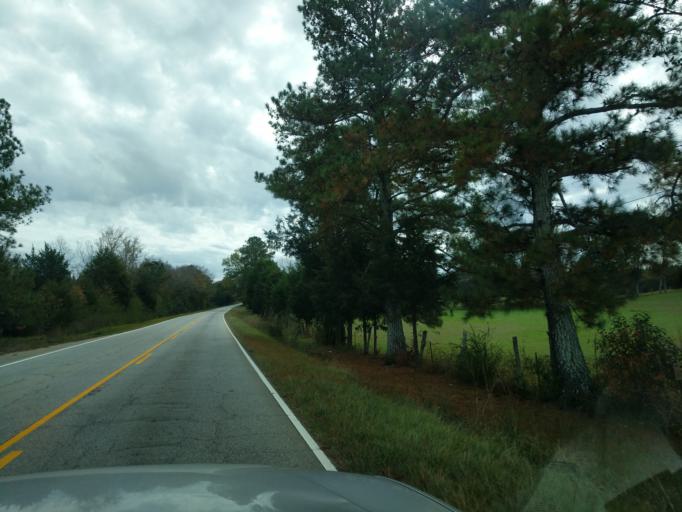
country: US
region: South Carolina
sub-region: Greenwood County
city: Ninety Six
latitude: 34.1642
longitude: -81.8556
